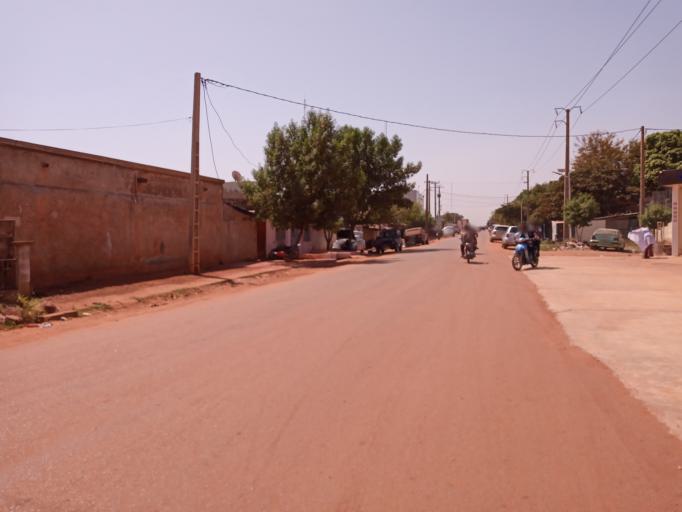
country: ML
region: Bamako
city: Bamako
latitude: 12.6138
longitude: -7.9934
